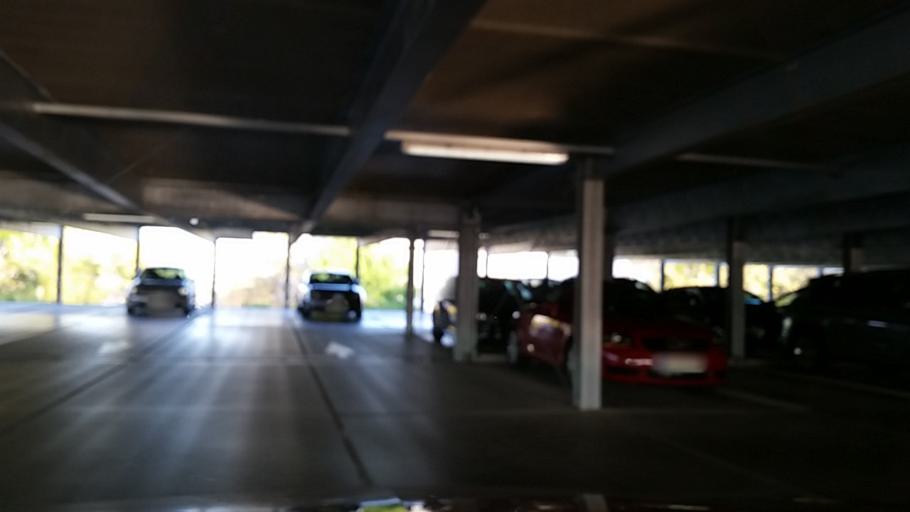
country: DE
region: Lower Saxony
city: Wolfsburg
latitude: 52.4305
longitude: 10.7612
